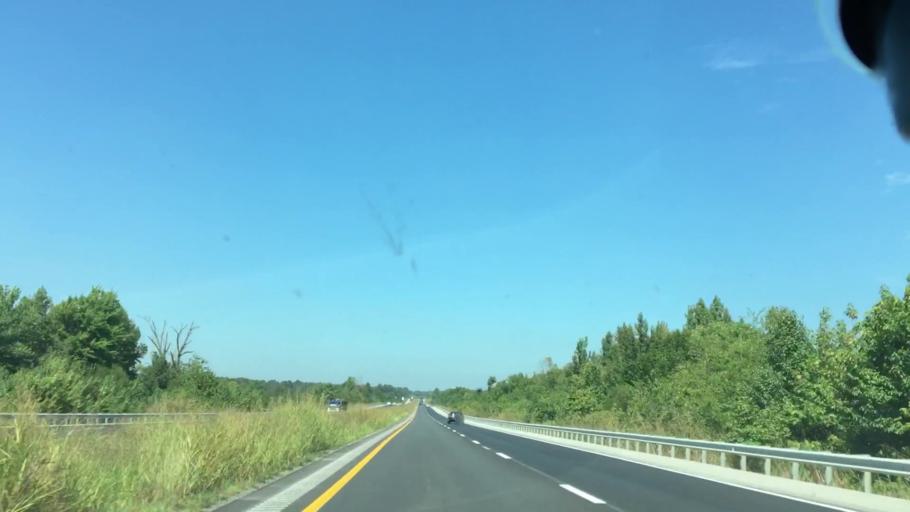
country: US
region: Kentucky
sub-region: Hopkins County
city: Madisonville
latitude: 37.4357
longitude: -87.4731
